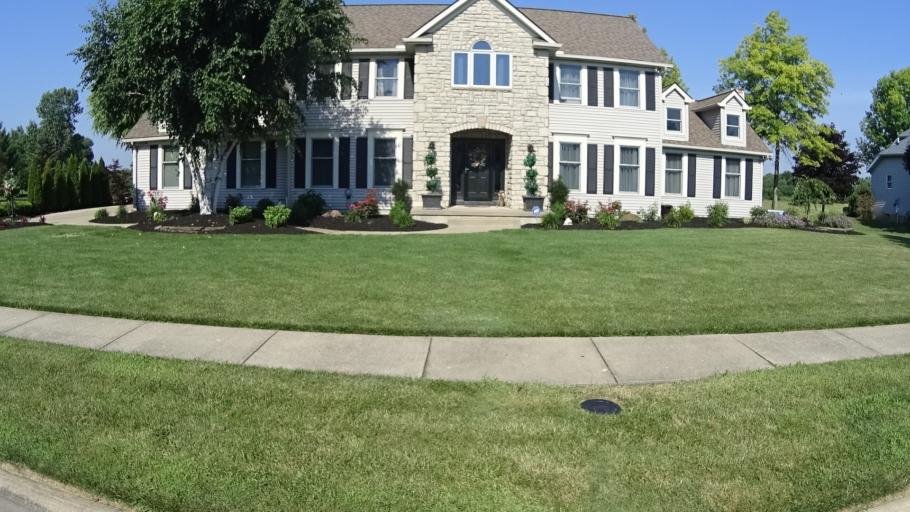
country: US
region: Ohio
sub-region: Erie County
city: Huron
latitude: 41.4035
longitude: -82.5741
